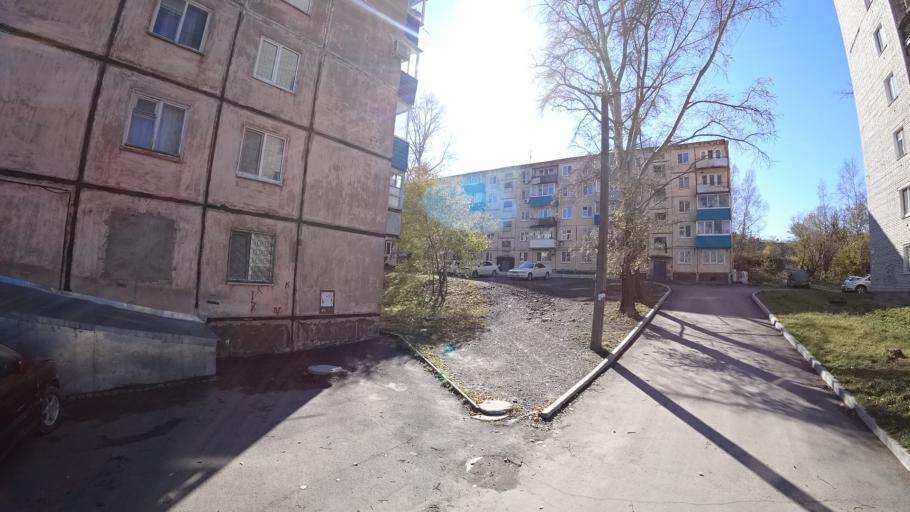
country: RU
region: Khabarovsk Krai
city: Amursk
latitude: 50.2208
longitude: 136.9087
